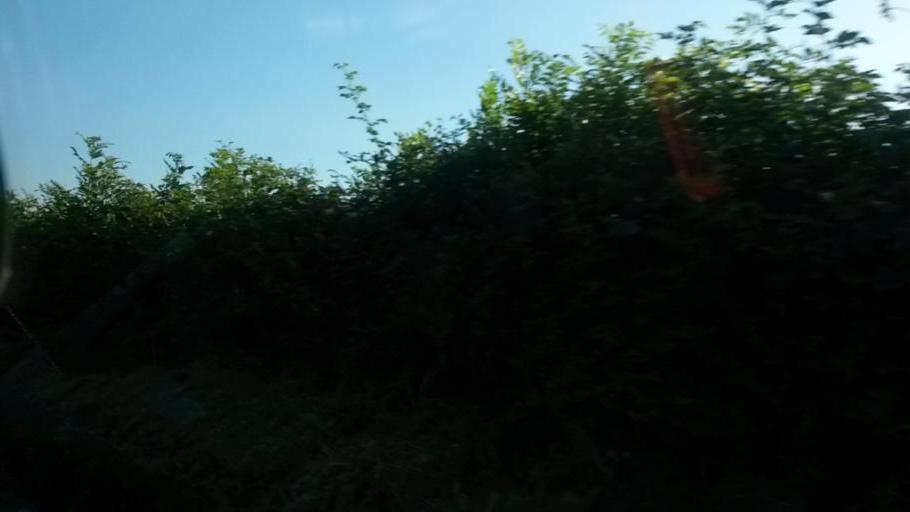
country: IE
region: Leinster
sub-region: An Mhi
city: Ashbourne
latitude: 53.5145
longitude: -6.3544
